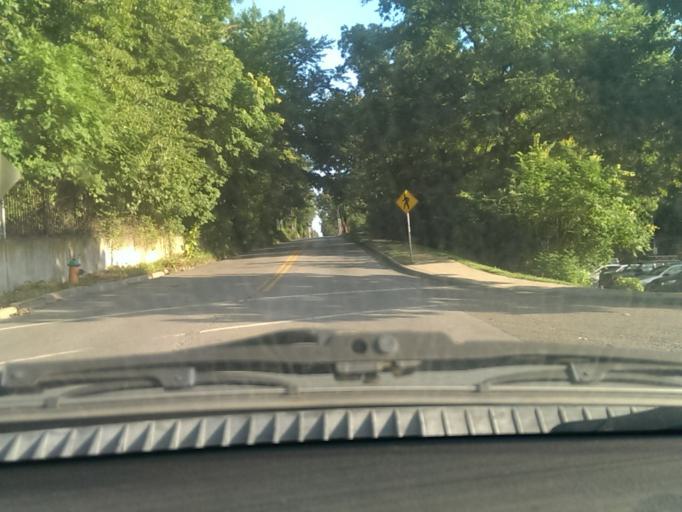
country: US
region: Kansas
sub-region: Johnson County
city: Westwood
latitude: 39.0307
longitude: -94.6075
